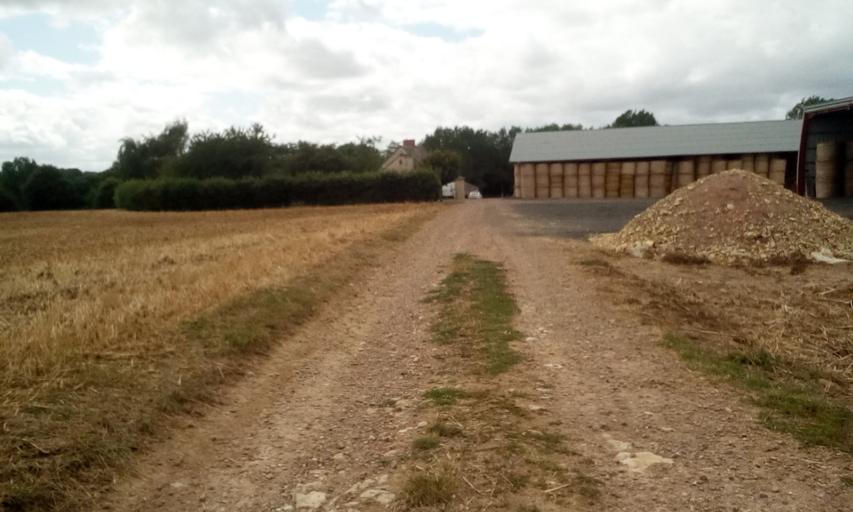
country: FR
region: Lower Normandy
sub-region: Departement du Calvados
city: Tilly-sur-Seulles
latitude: 49.2047
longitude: -0.6275
